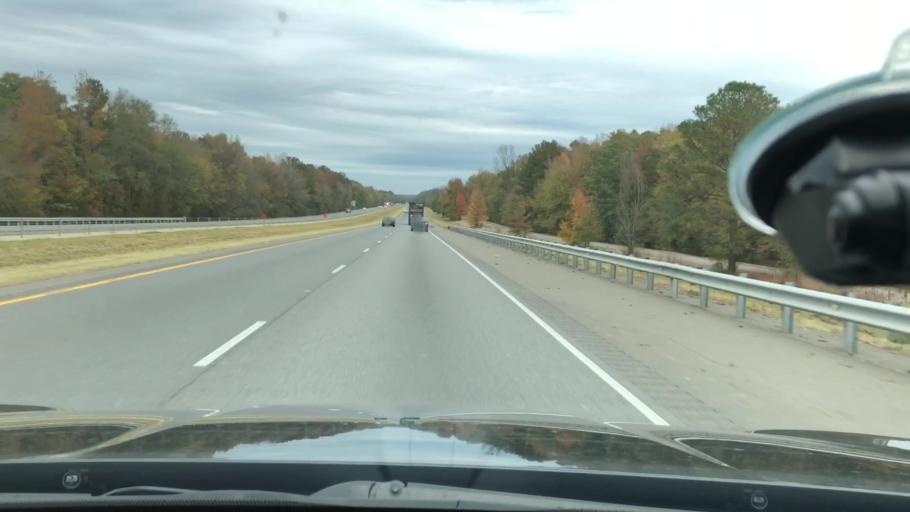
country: US
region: Arkansas
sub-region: Hot Spring County
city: Malvern
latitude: 34.3587
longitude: -92.8791
